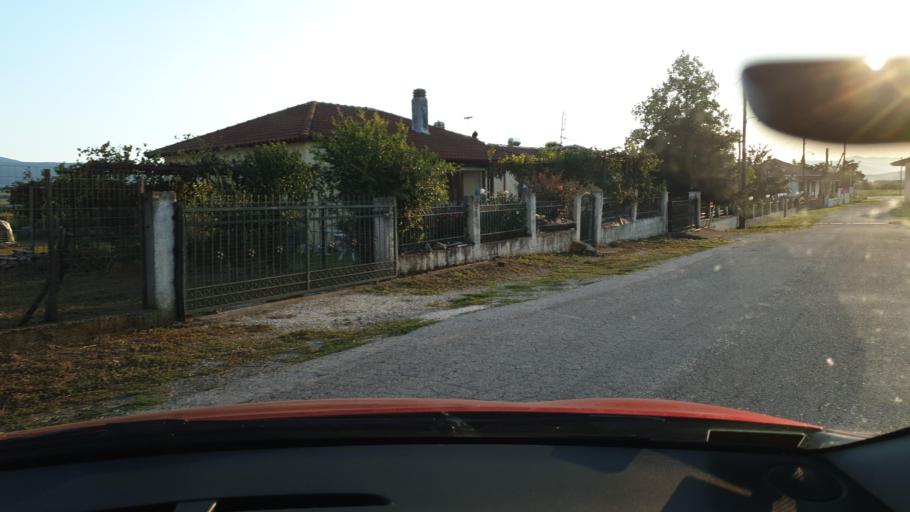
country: GR
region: Central Macedonia
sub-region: Nomos Thessalonikis
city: Nea Apollonia
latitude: 40.5574
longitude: 23.4730
